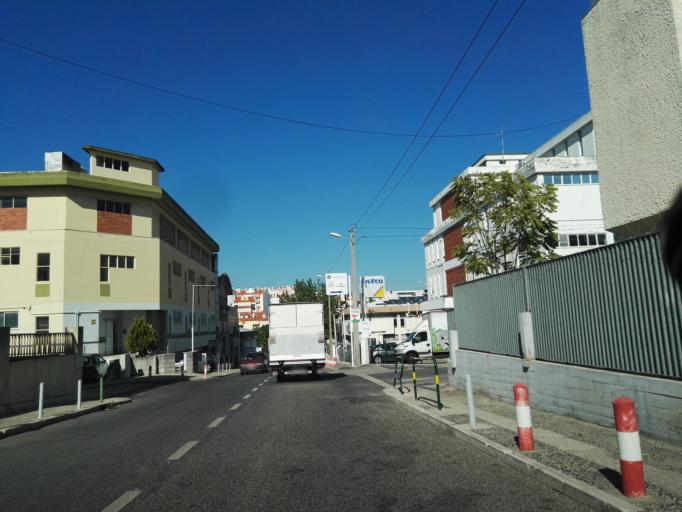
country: PT
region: Lisbon
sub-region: Loures
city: Sacavem
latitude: 38.7877
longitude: -9.1202
